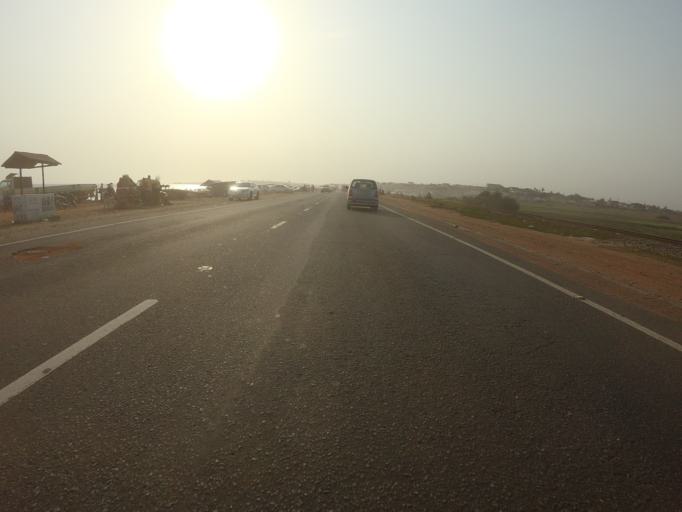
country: GH
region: Greater Accra
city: Nungua
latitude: 5.6126
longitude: -0.0403
